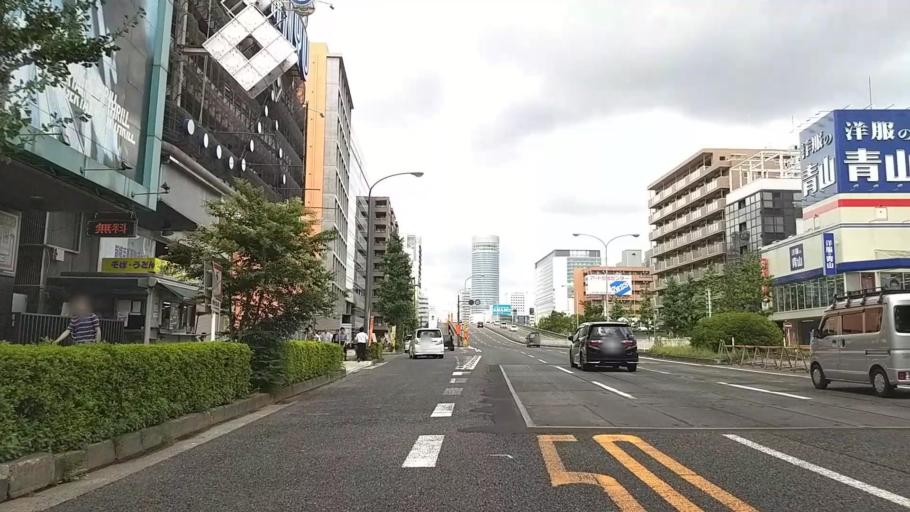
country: JP
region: Kanagawa
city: Yokohama
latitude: 35.5046
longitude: 139.6114
